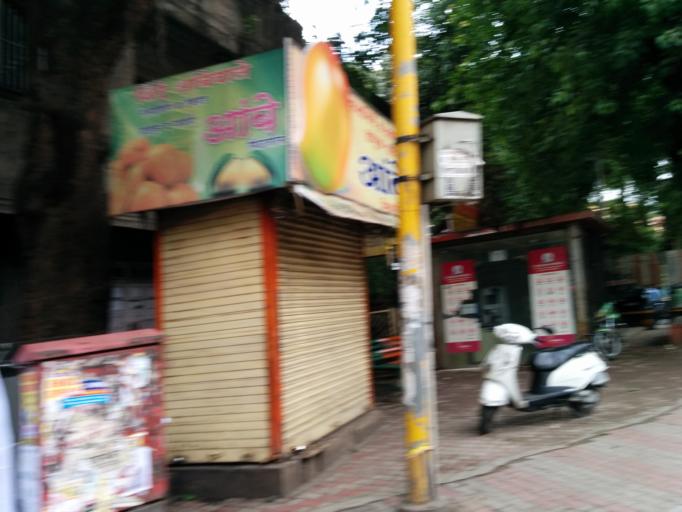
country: IN
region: Maharashtra
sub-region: Pune Division
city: Pune
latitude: 18.5076
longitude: 73.8508
